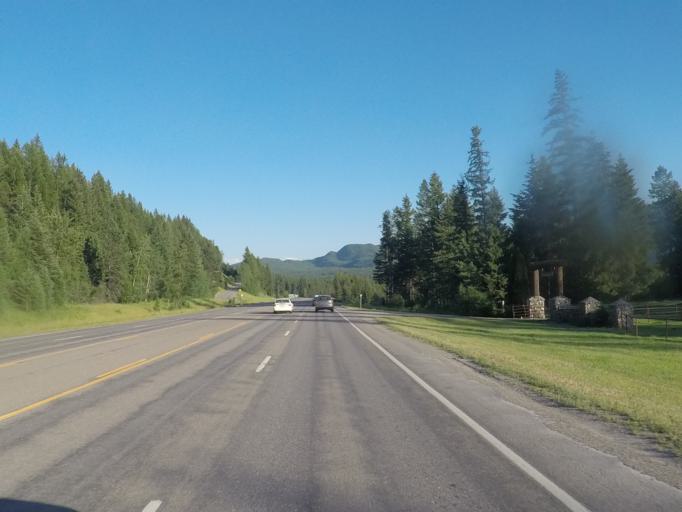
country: US
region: Montana
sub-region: Flathead County
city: Columbia Falls
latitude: 48.4103
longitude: -114.0478
